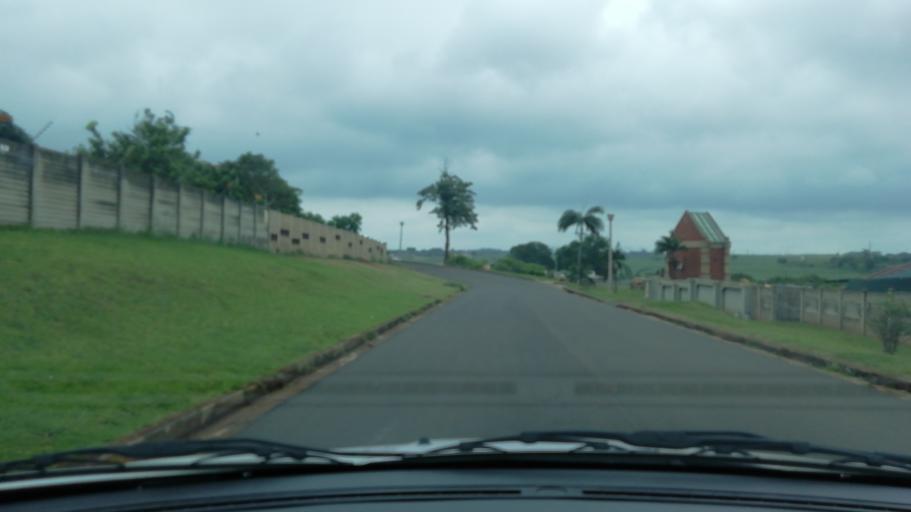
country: ZA
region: KwaZulu-Natal
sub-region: uThungulu District Municipality
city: Empangeni
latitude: -28.7627
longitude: 31.9045
